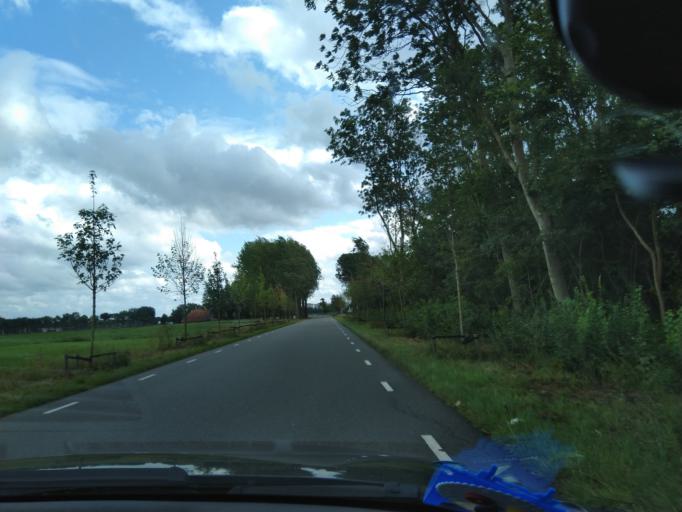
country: NL
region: Groningen
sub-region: Gemeente Zuidhorn
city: Aduard
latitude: 53.2392
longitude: 6.4950
